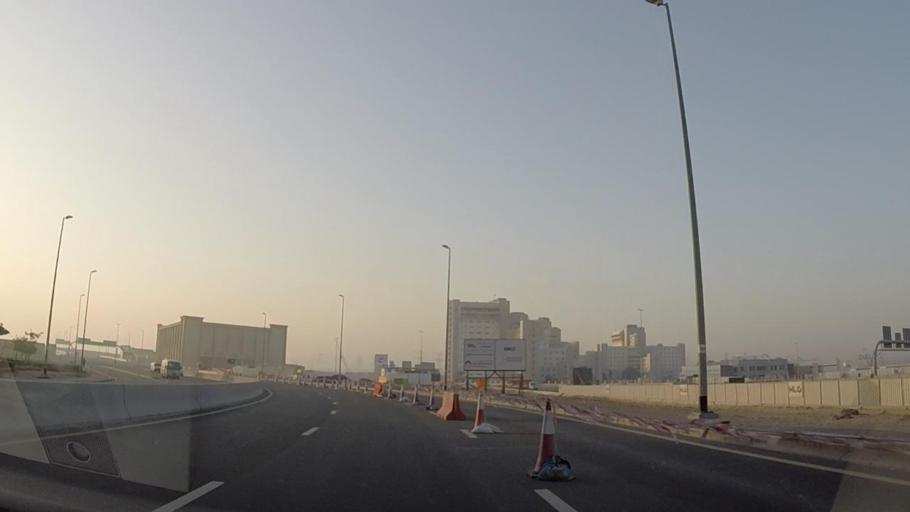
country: AE
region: Dubai
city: Dubai
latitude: 25.0627
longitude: 55.1369
